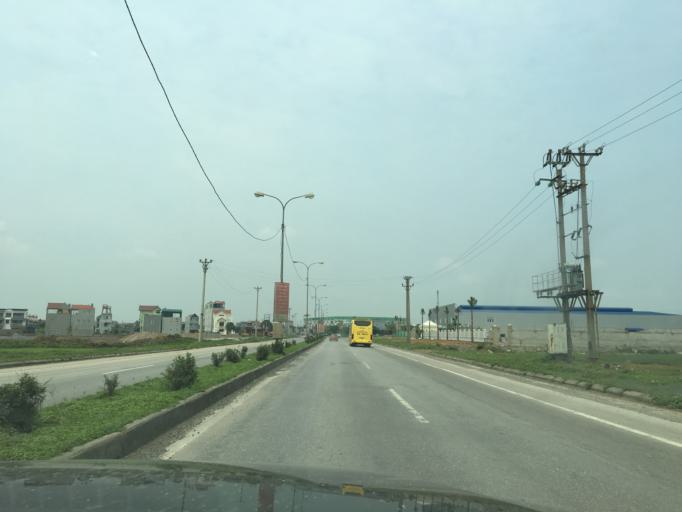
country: VN
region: Ninh Binh
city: Thanh Pho Ninh Binh
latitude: 20.2380
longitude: 106.0002
